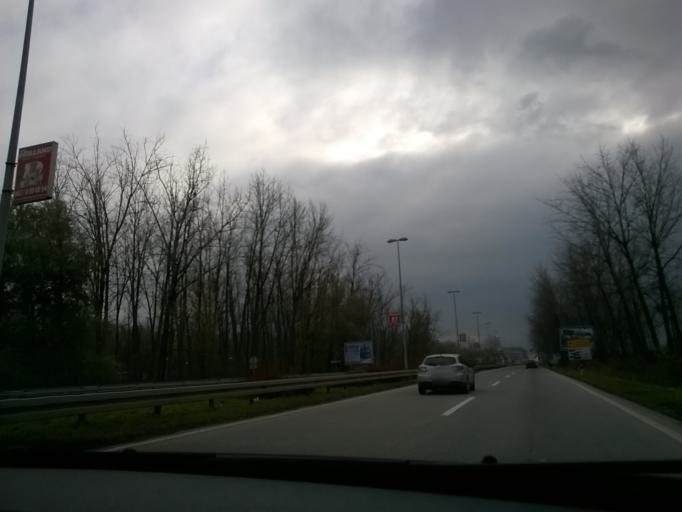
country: RS
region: Autonomna Pokrajina Vojvodina
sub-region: Juznobacki Okrug
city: Novi Sad
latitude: 45.2825
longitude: 19.8511
